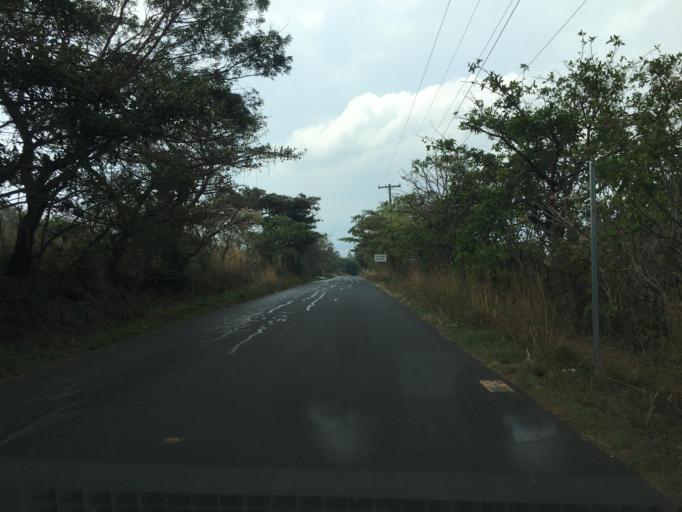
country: GT
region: Escuintla
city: San Vicente Pacaya
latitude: 14.3275
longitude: -90.5632
